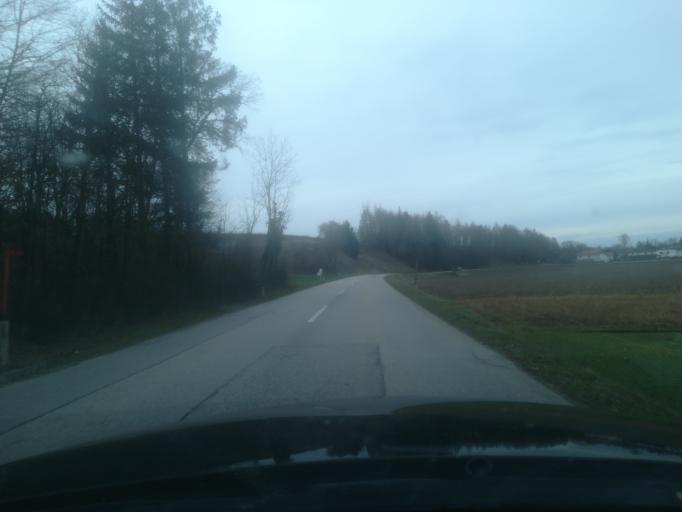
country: AT
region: Upper Austria
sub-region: Wels-Land
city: Gunskirchen
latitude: 48.0817
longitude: 13.9530
